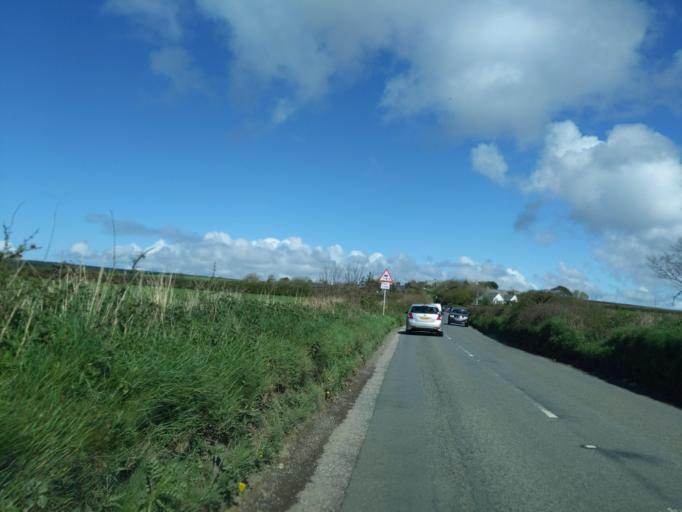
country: GB
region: England
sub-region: Cornwall
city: Wadebridge
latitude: 50.5787
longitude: -4.7986
